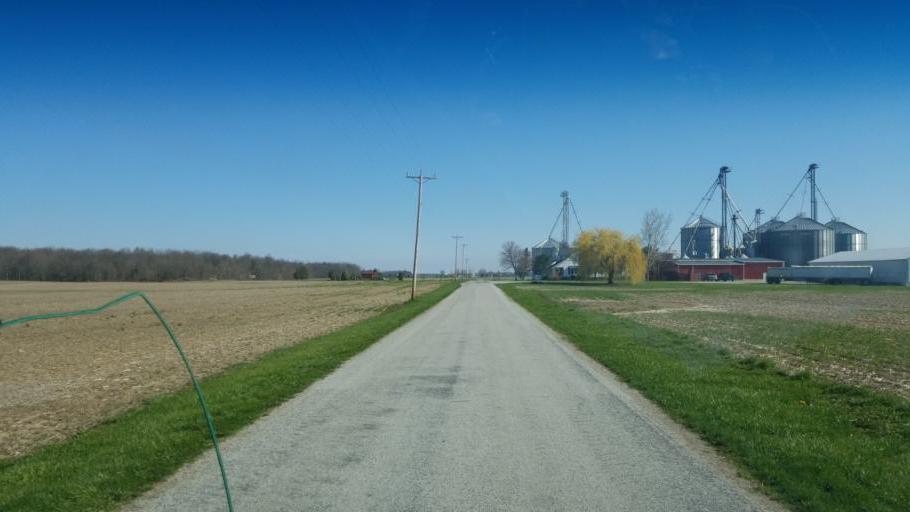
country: US
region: Ohio
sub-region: Hardin County
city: Kenton
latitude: 40.6744
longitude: -83.5618
